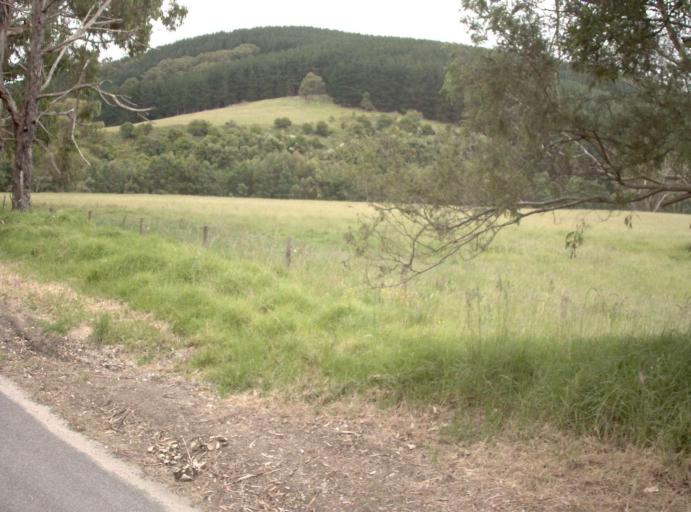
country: AU
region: Victoria
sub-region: Latrobe
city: Traralgon
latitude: -38.4856
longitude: 146.6070
